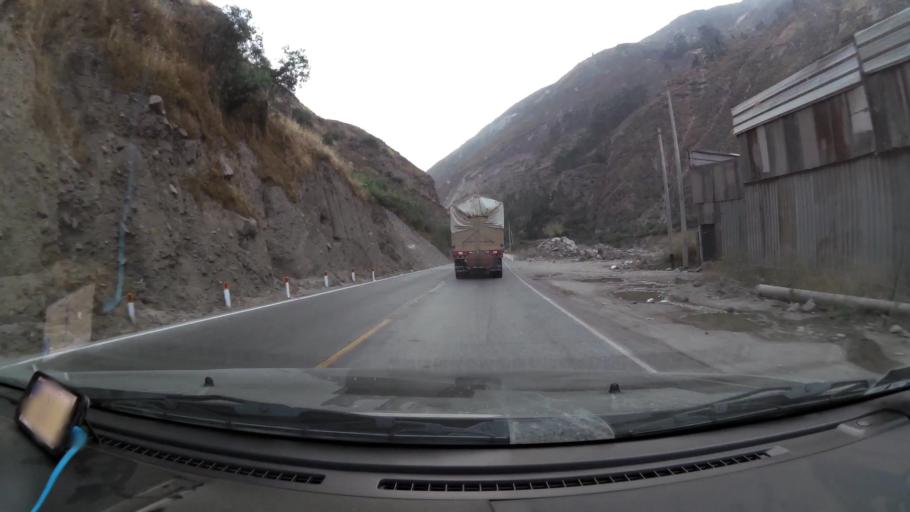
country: PE
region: Lima
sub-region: Provincia de Huarochiri
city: Matucana
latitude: -11.8241
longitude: -76.3647
